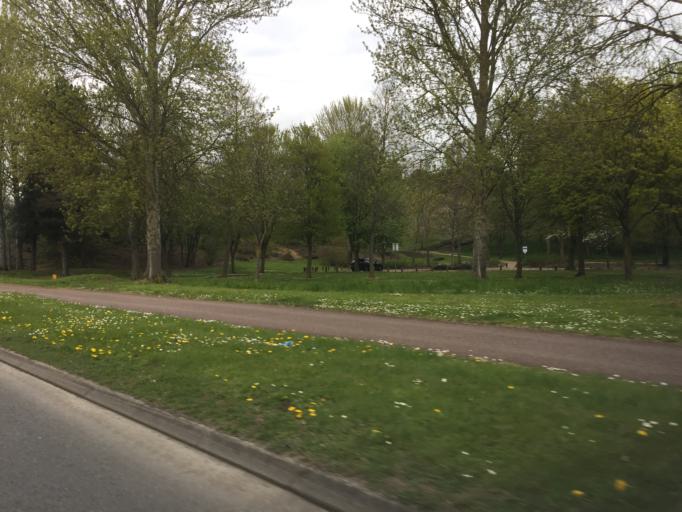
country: GB
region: England
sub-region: Milton Keynes
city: Newport Pagnell
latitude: 52.0571
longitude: -0.7288
